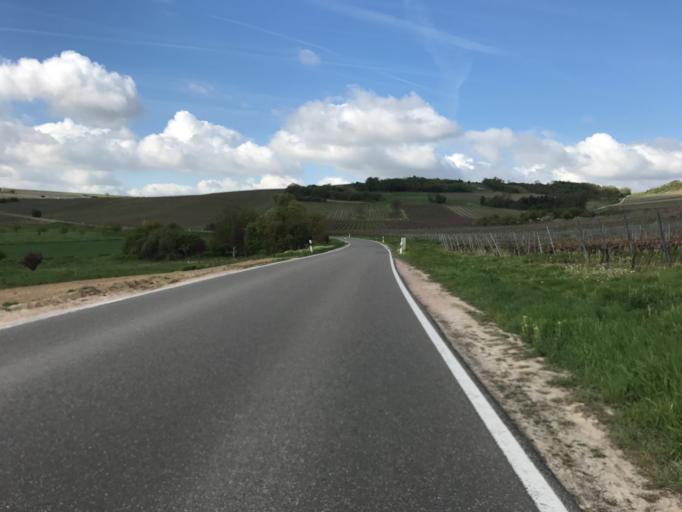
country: DE
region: Rheinland-Pfalz
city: Bubenheim
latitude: 49.9148
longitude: 8.0795
